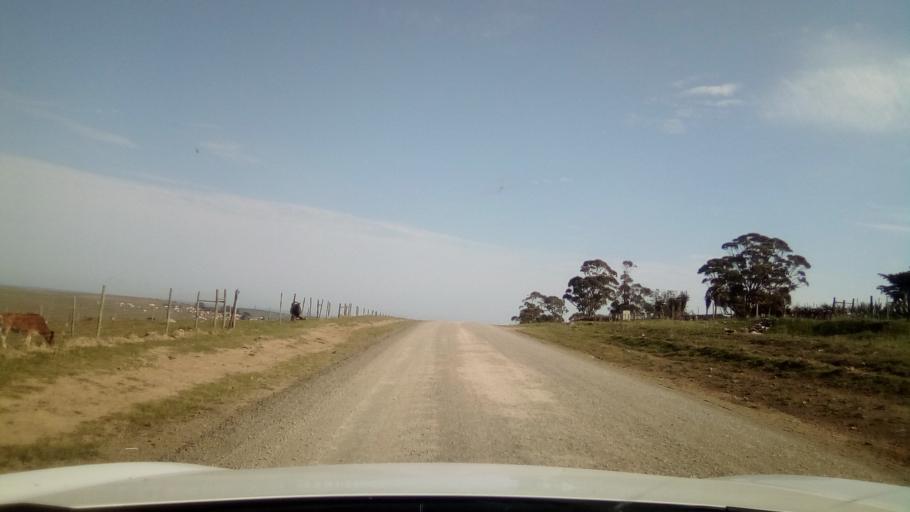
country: ZA
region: Eastern Cape
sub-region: Buffalo City Metropolitan Municipality
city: Bhisho
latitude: -32.9862
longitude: 27.2600
